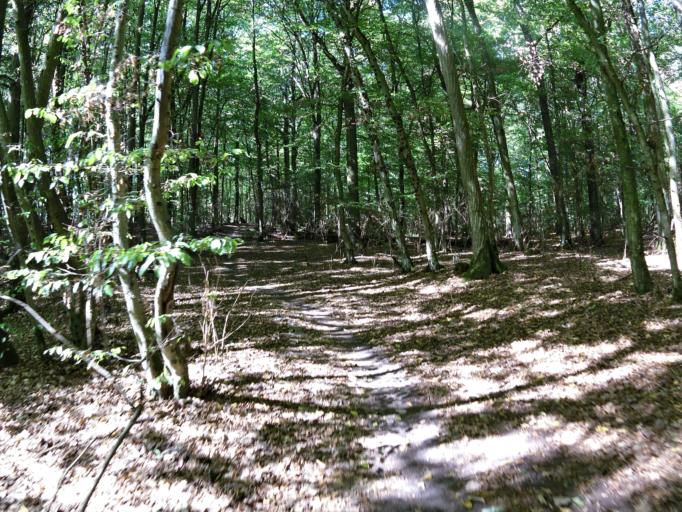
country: DE
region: Bavaria
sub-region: Regierungsbezirk Unterfranken
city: Eisingen
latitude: 49.7670
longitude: 9.8492
